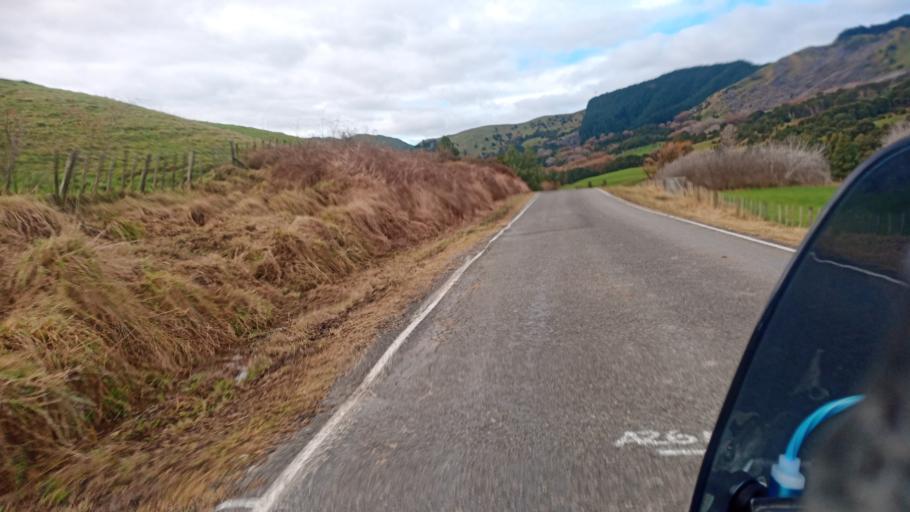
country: NZ
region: Gisborne
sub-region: Gisborne District
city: Gisborne
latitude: -38.4350
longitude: 177.9030
